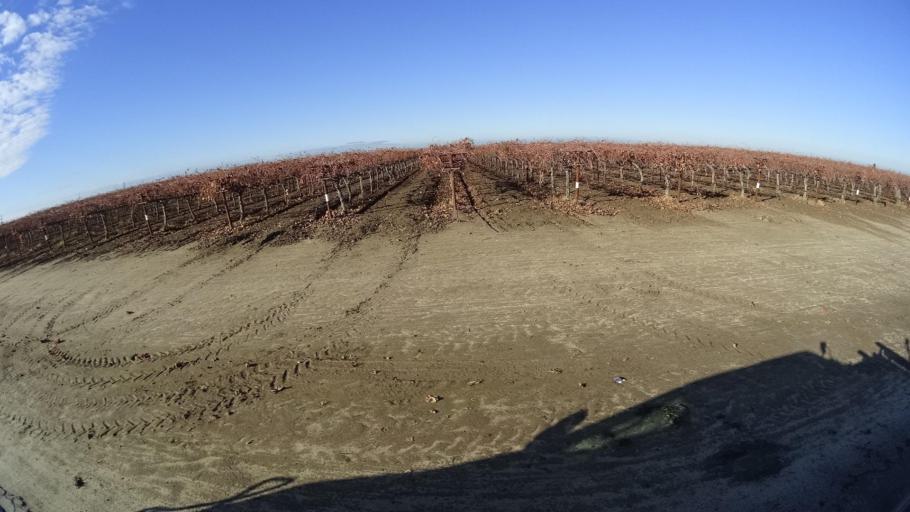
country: US
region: California
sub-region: Kern County
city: Delano
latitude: 35.7204
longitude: -119.2942
